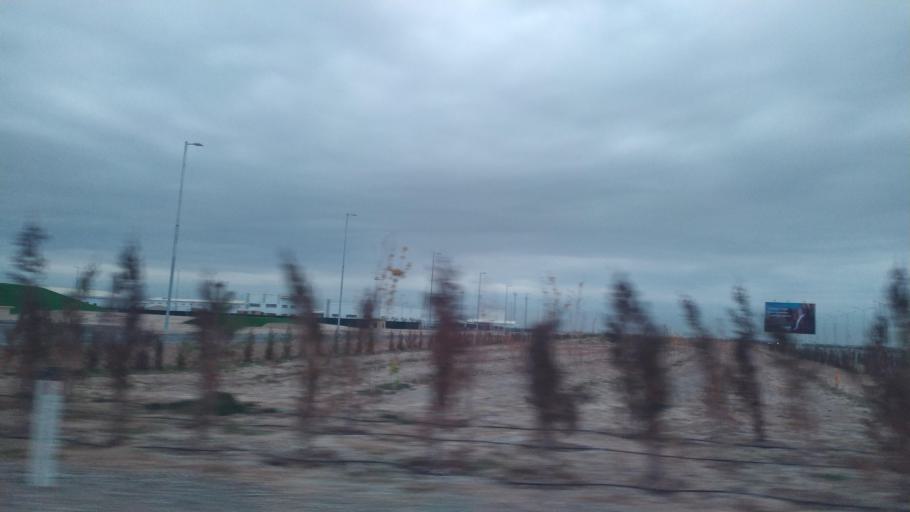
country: KZ
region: Ongtustik Qazaqstan
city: Kentau
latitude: 43.3173
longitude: 68.5450
